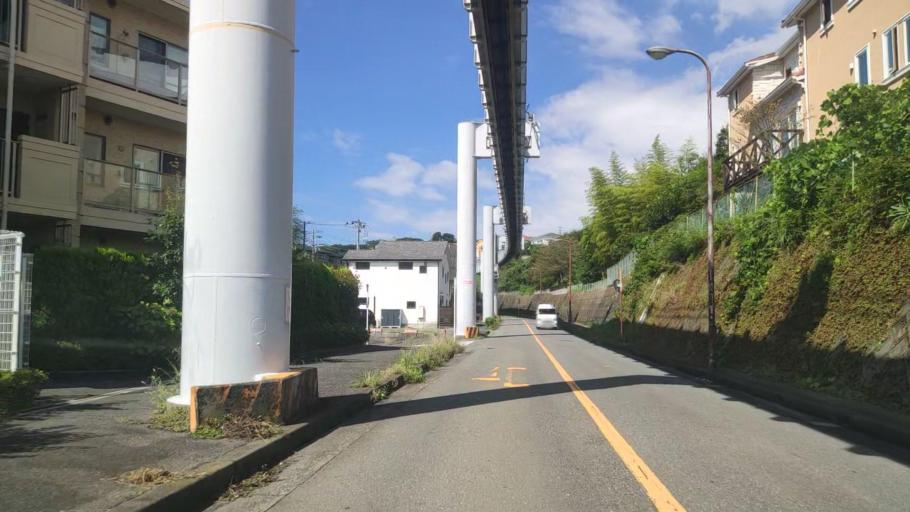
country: JP
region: Kanagawa
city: Fujisawa
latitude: 35.3198
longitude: 139.5014
